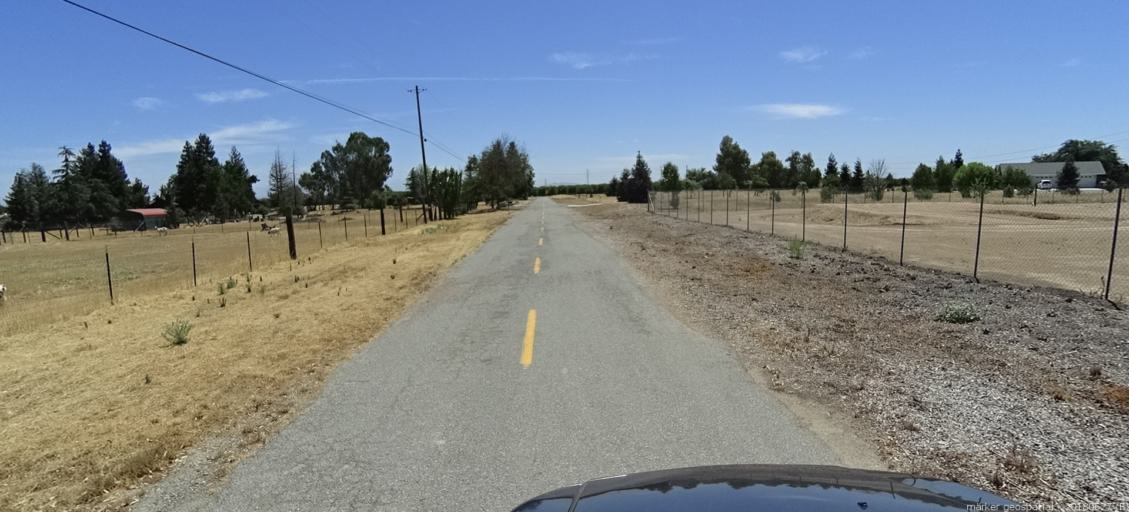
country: US
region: California
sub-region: Madera County
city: Bonadelle Ranchos-Madera Ranchos
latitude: 36.9358
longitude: -119.8608
